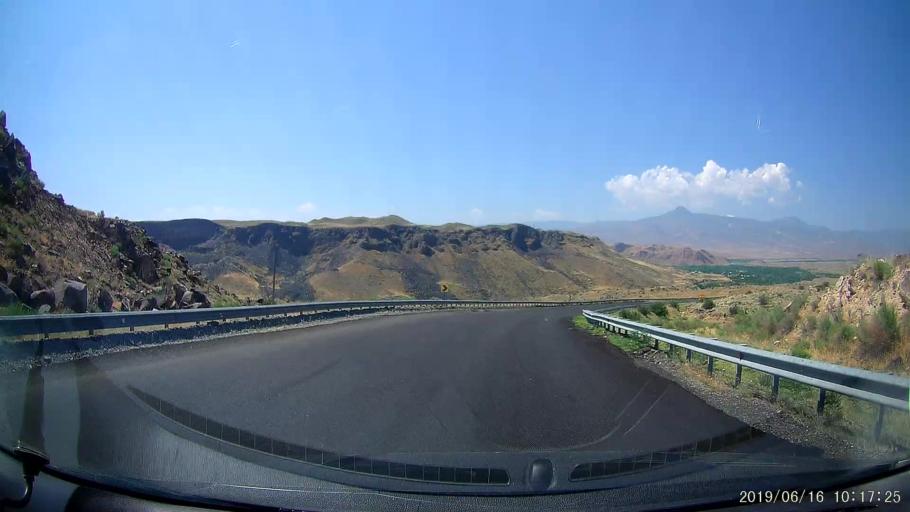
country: TR
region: Igdir
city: Tuzluca
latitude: 40.1681
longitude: 43.6824
